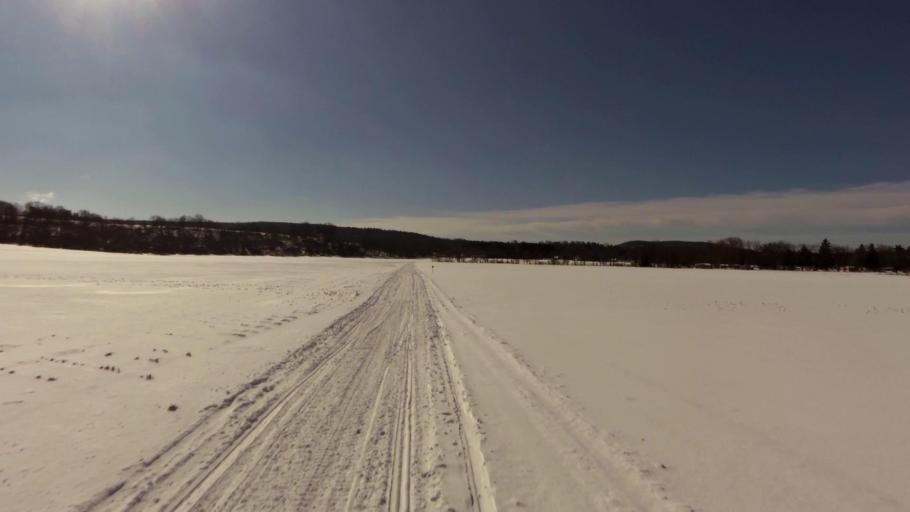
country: US
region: New York
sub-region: Cattaraugus County
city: Franklinville
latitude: 42.3524
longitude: -78.4505
